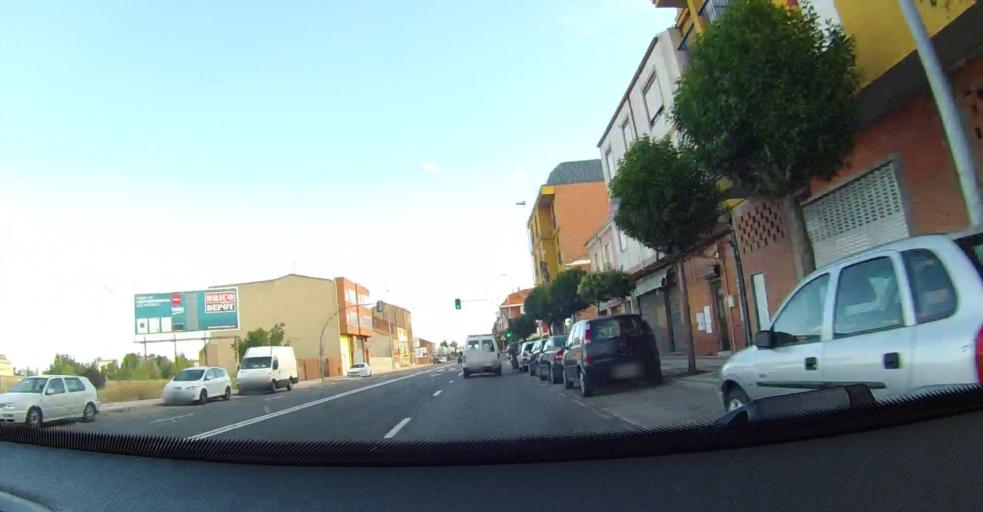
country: ES
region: Castille and Leon
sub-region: Provincia de Leon
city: Leon
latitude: 42.5881
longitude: -5.5845
